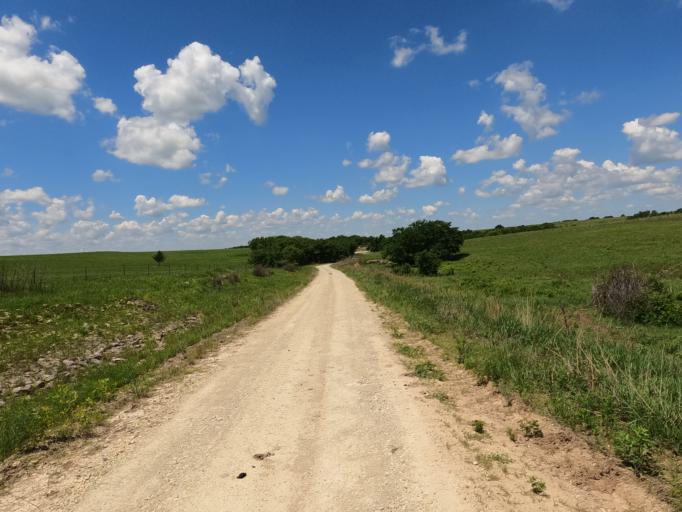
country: US
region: Kansas
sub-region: Marion County
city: Marion
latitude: 38.2414
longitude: -96.7990
